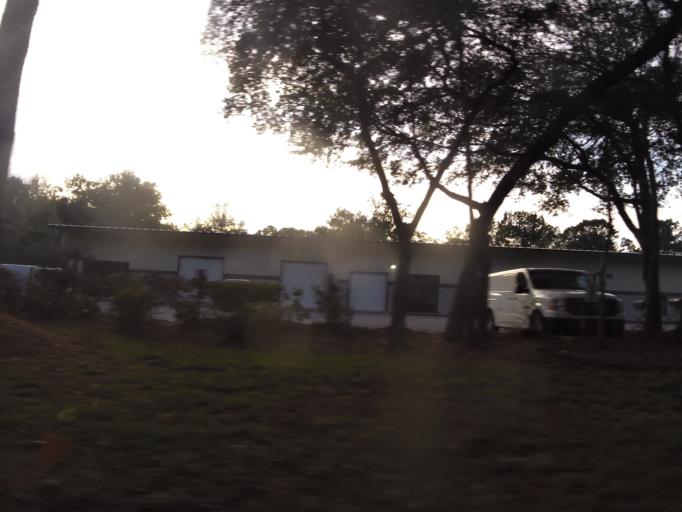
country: US
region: Florida
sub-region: Saint Johns County
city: Fruit Cove
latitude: 30.1599
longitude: -81.5392
